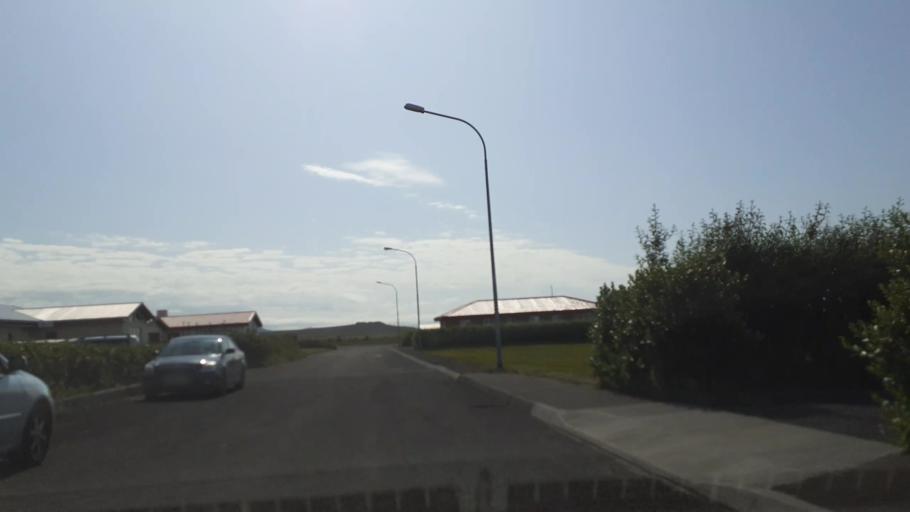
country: IS
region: Northwest
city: Saudarkrokur
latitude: 65.8216
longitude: -20.3000
